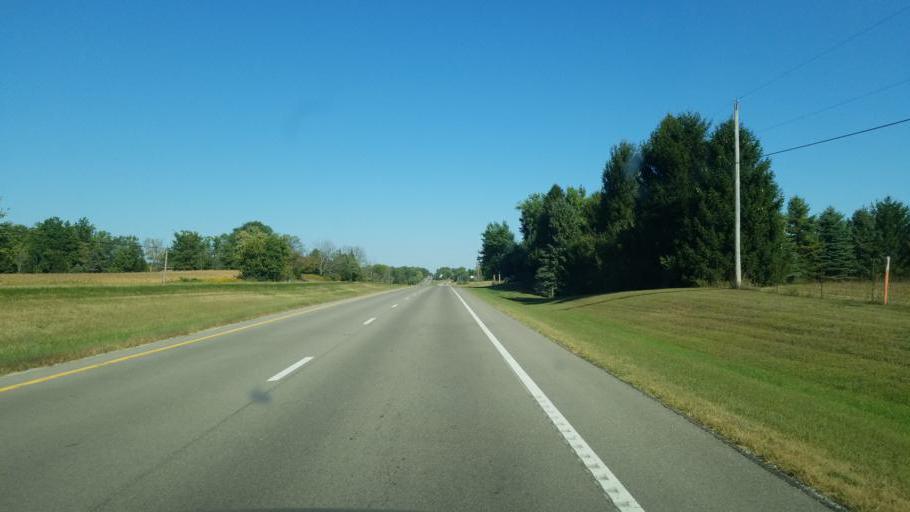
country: US
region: Ohio
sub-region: Clark County
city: Lisbon
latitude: 39.9290
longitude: -83.5798
